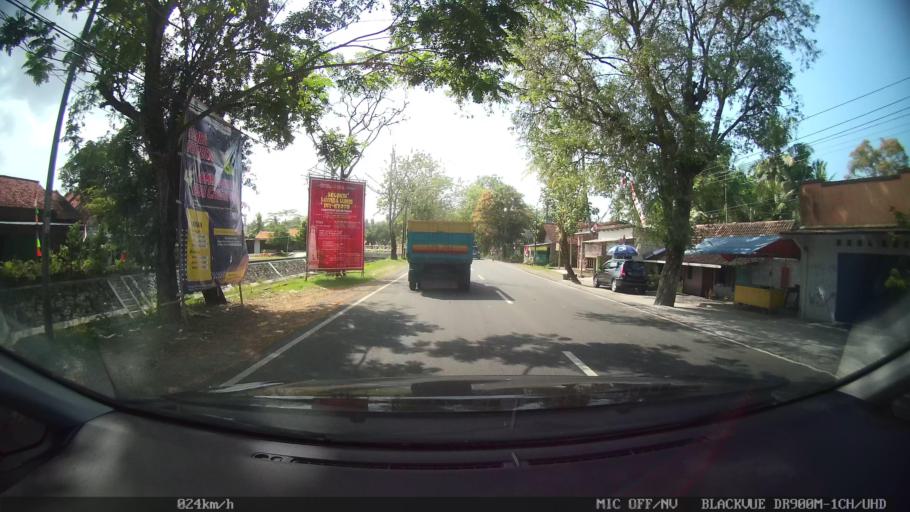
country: ID
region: Daerah Istimewa Yogyakarta
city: Srandakan
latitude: -7.8956
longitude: 110.1531
